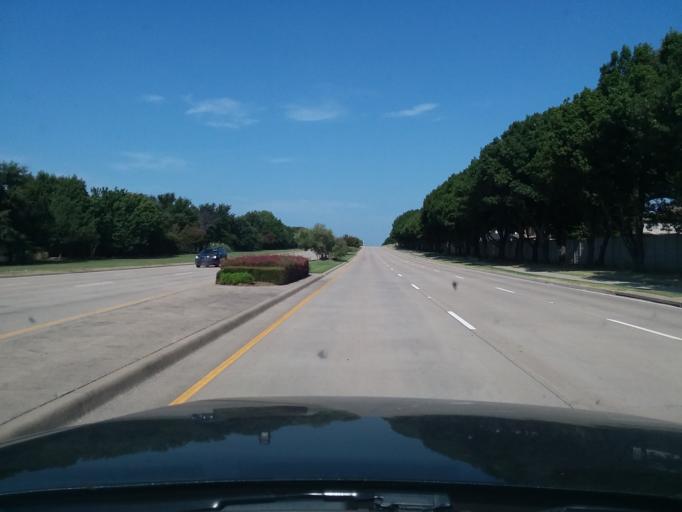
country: US
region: Texas
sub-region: Denton County
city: Flower Mound
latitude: 33.0138
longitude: -97.0627
